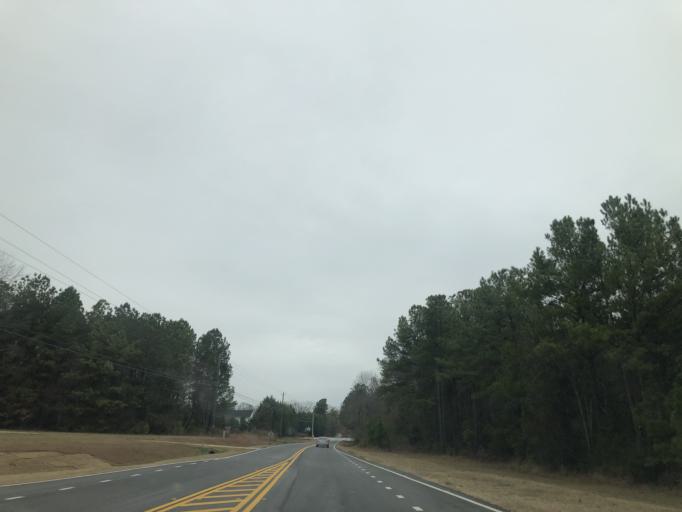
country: US
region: Georgia
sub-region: Clayton County
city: Conley
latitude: 33.6270
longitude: -84.2568
